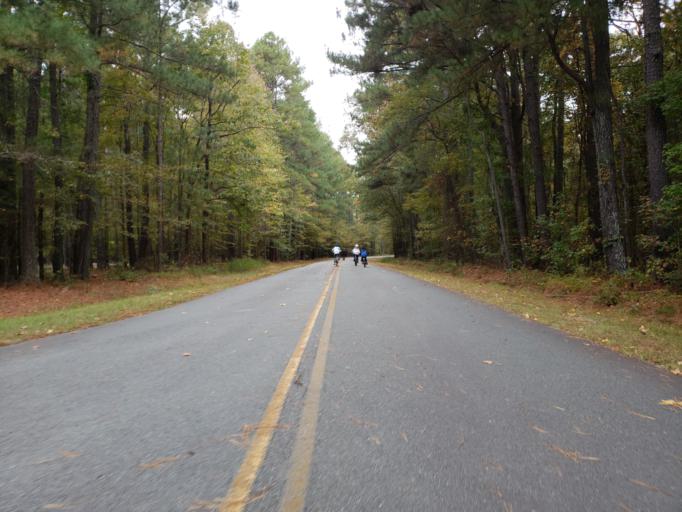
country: US
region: North Carolina
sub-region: Chatham County
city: Fearrington Village
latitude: 35.7491
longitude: -79.0394
